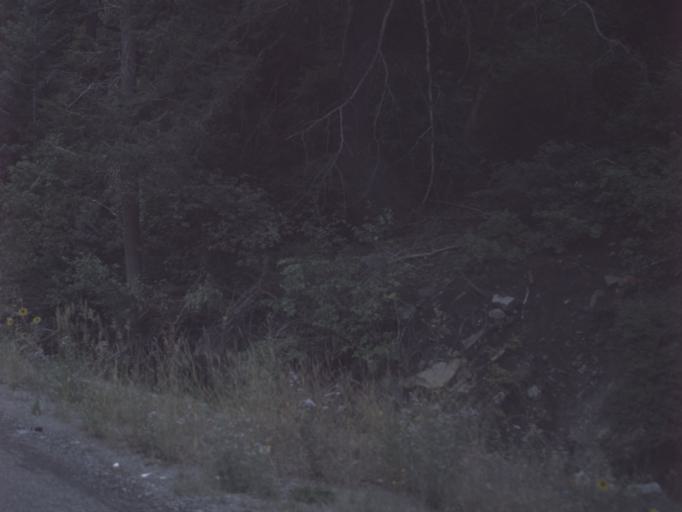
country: US
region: Utah
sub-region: Utah County
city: Orem
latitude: 40.3738
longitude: -111.5688
